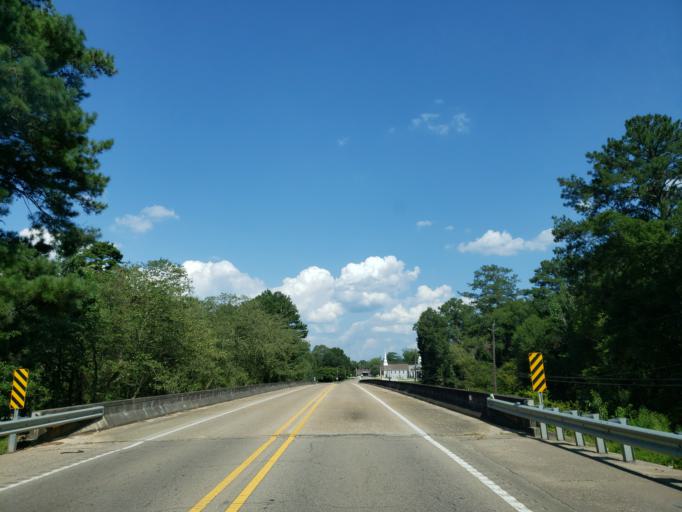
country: US
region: Mississippi
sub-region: Covington County
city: Collins
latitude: 31.5630
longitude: -89.5055
